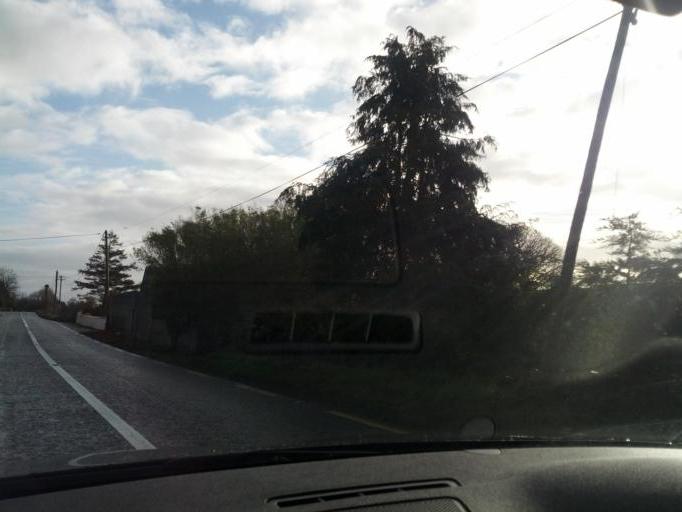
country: IE
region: Connaught
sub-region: County Galway
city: Athenry
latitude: 53.3359
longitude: -8.8116
